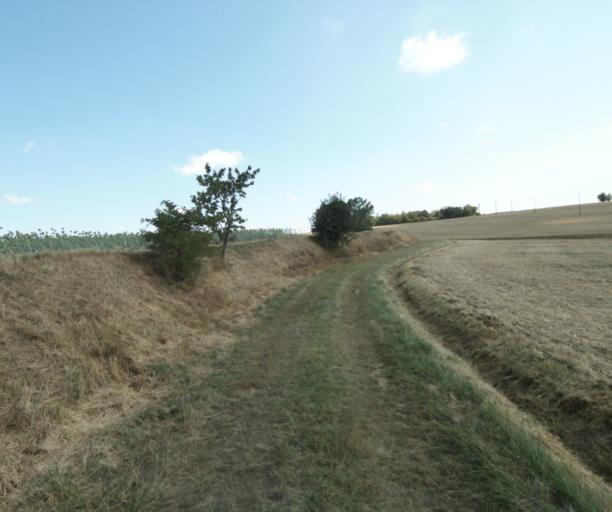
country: FR
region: Midi-Pyrenees
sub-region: Departement de la Haute-Garonne
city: Auriac-sur-Vendinelle
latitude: 43.4486
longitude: 1.7952
